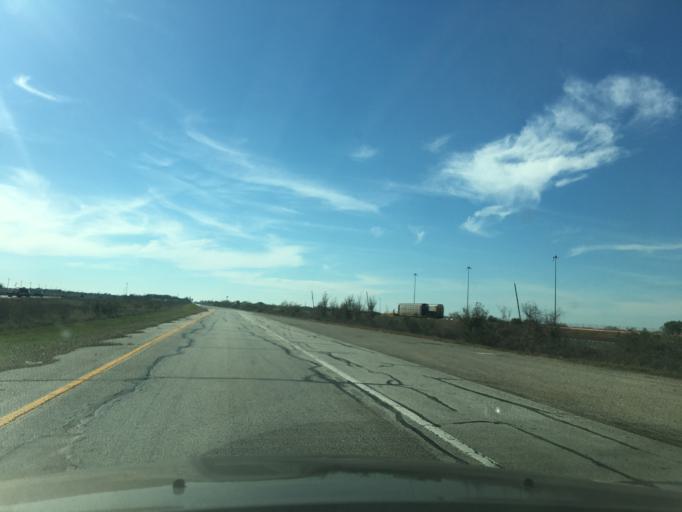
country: US
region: Texas
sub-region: Wharton County
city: East Bernard
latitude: 29.4612
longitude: -95.9775
